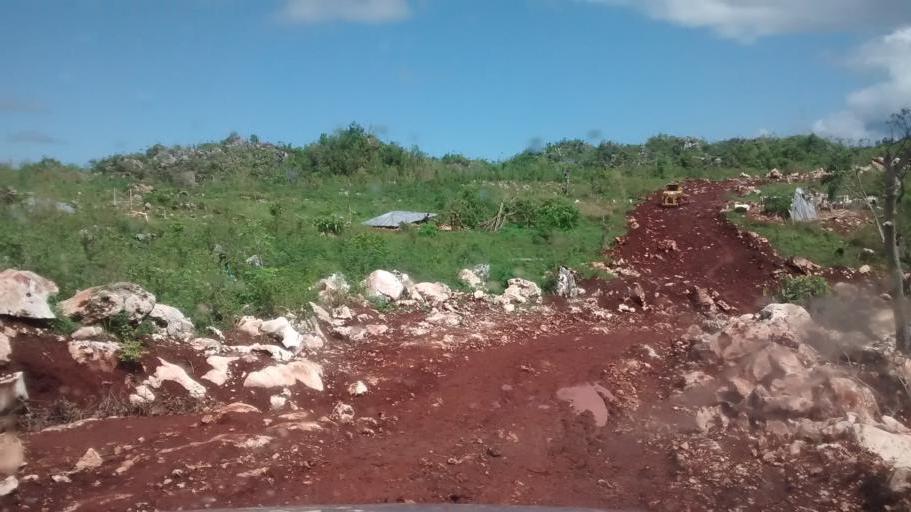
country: HT
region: Grandans
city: Corail
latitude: 18.5403
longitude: -73.9235
